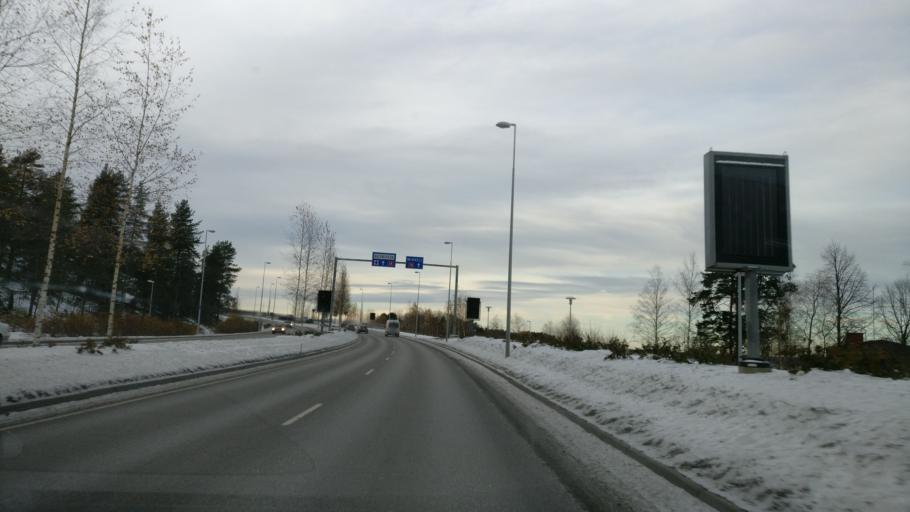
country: FI
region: Southern Savonia
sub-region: Savonlinna
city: Savonlinna
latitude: 61.8701
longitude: 28.9179
